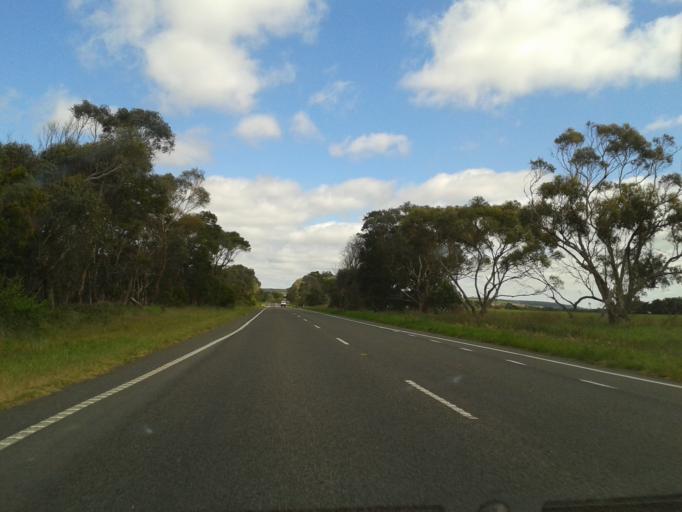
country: AU
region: Victoria
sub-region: Glenelg
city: Portland
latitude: -38.2183
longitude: 141.7947
